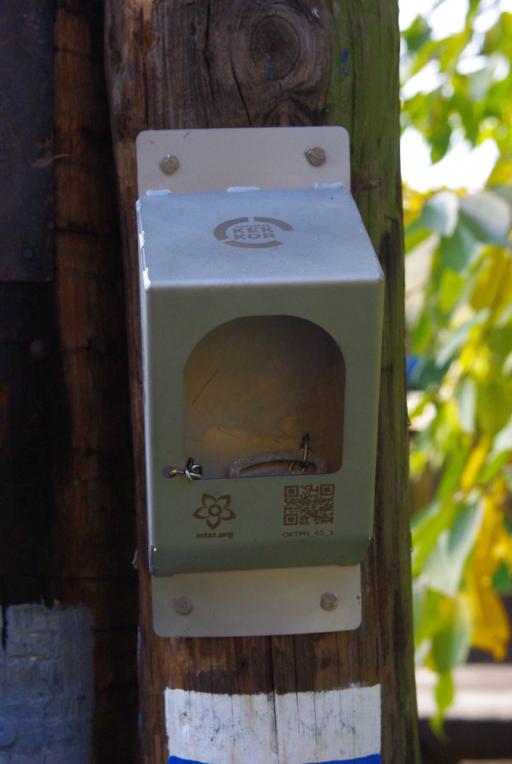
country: HU
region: Komarom-Esztergom
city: Piliscsev
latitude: 47.7010
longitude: 18.8350
